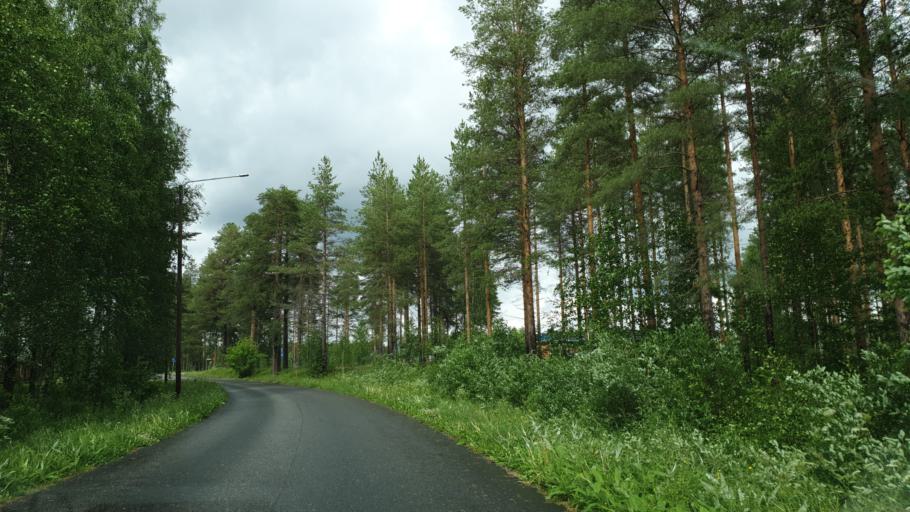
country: FI
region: Kainuu
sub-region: Kehys-Kainuu
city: Kuhmo
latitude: 64.1164
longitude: 29.5174
